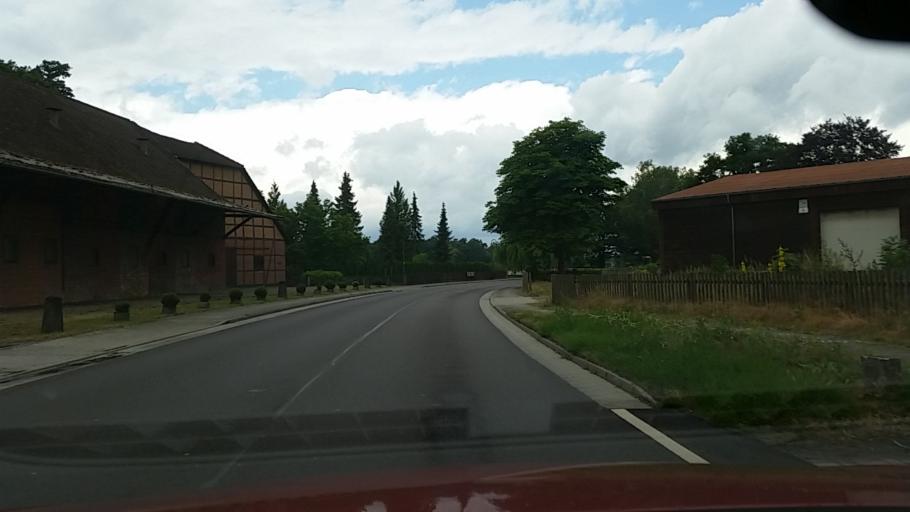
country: DE
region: Lower Saxony
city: Sassenburg
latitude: 52.4862
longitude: 10.6320
